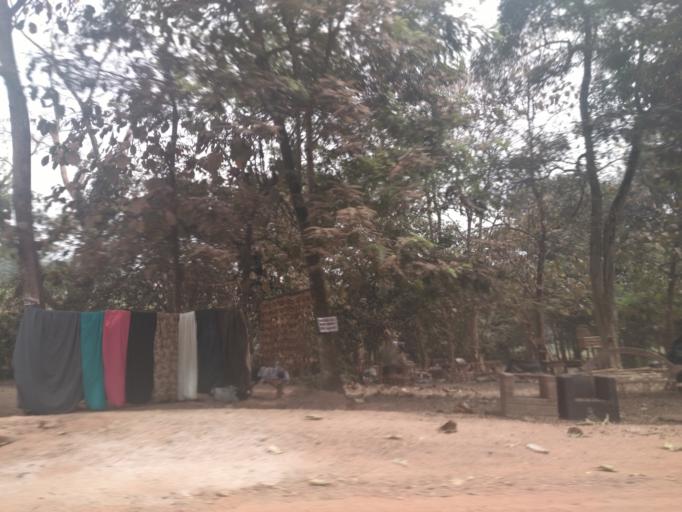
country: GH
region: Ashanti
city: Kumasi
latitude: 6.6824
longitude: -1.6227
